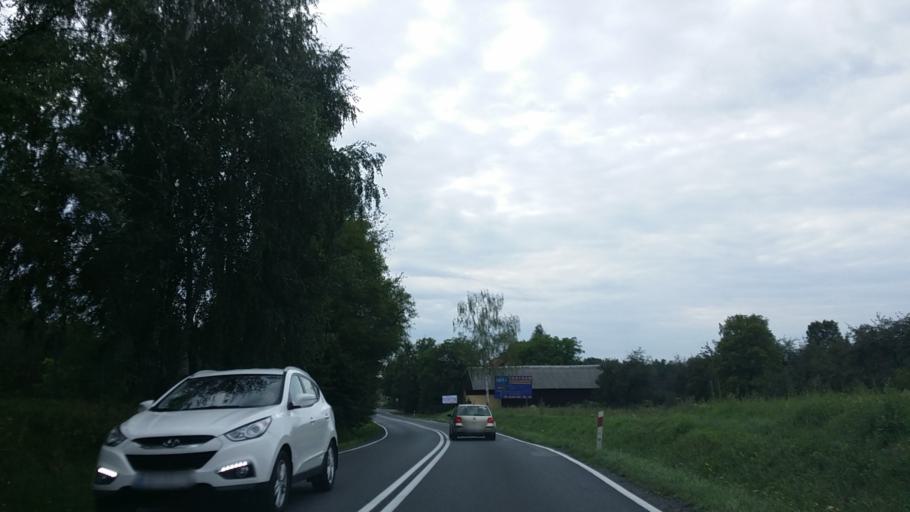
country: PL
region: Lesser Poland Voivodeship
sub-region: Powiat wadowicki
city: Brzeznica
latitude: 49.9623
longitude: 19.6518
